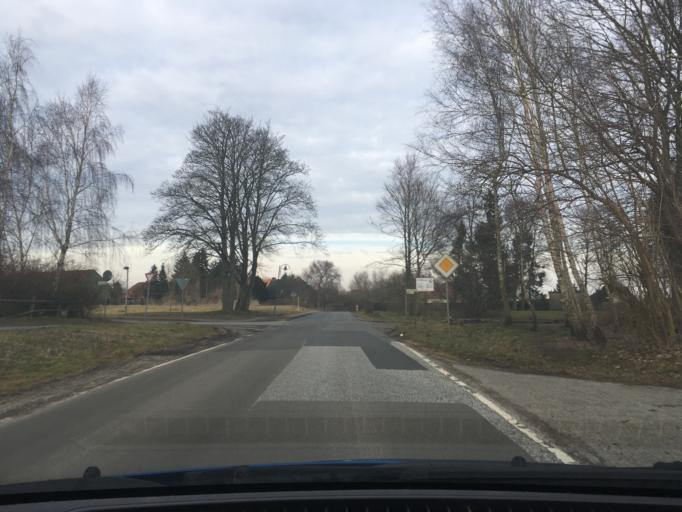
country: DE
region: Mecklenburg-Vorpommern
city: Klein Rogahn
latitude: 53.5943
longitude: 11.3219
